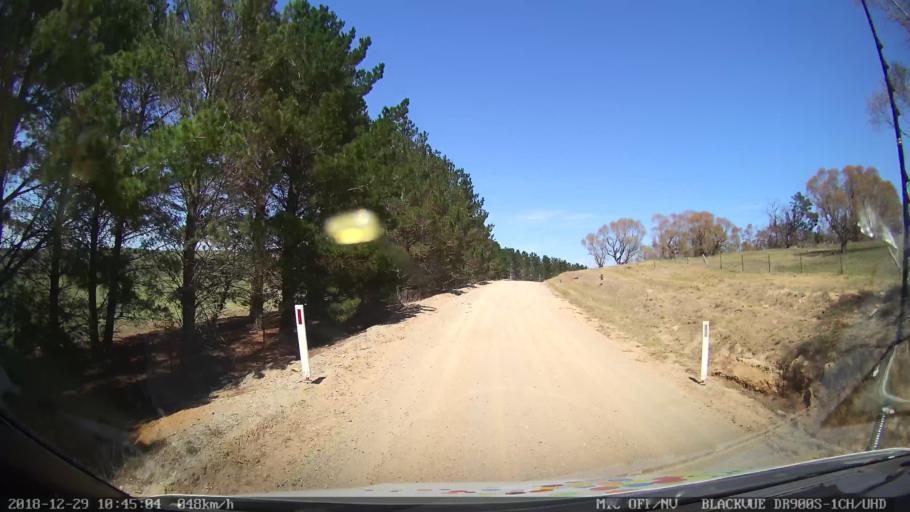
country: AU
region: New South Wales
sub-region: Palerang
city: Bungendore
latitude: -35.0454
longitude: 149.5240
